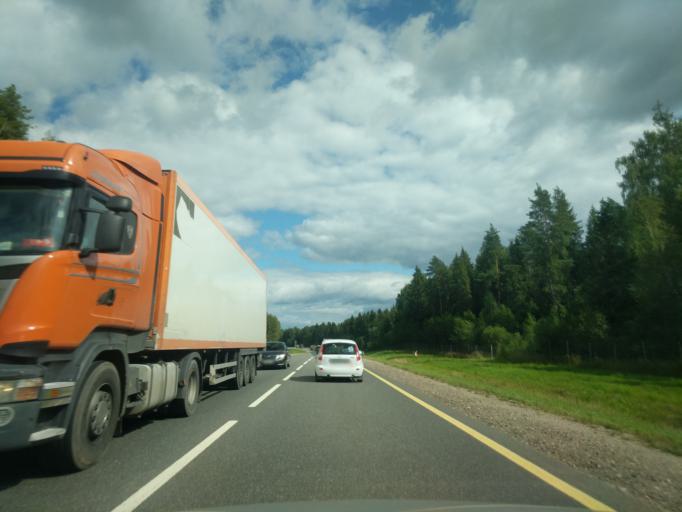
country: RU
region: Kostroma
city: Oktyabr'skiy
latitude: 57.7984
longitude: 41.2550
